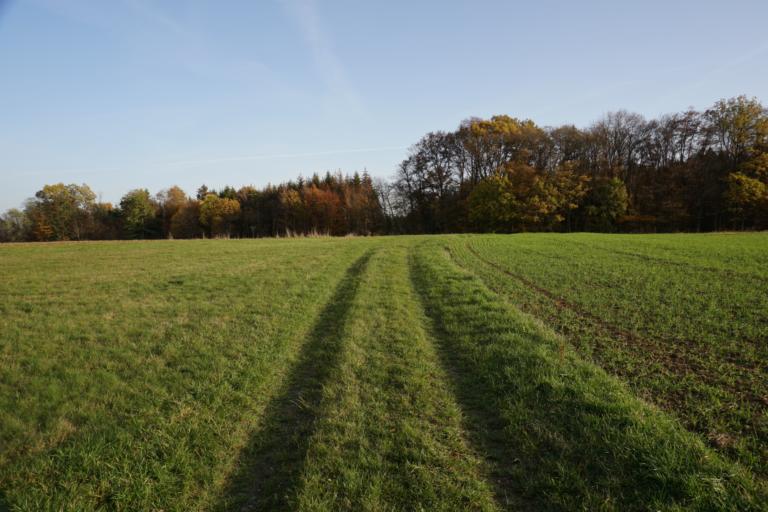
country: DE
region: Baden-Wuerttemberg
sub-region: Karlsruhe Region
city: Limbach
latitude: 49.4251
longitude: 9.2169
